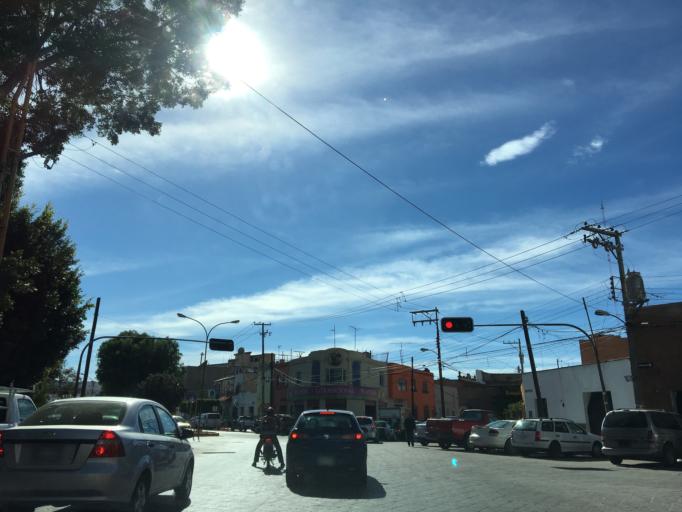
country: MX
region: San Luis Potosi
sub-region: San Luis Potosi
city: San Luis Potosi
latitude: 22.1493
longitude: -100.9828
